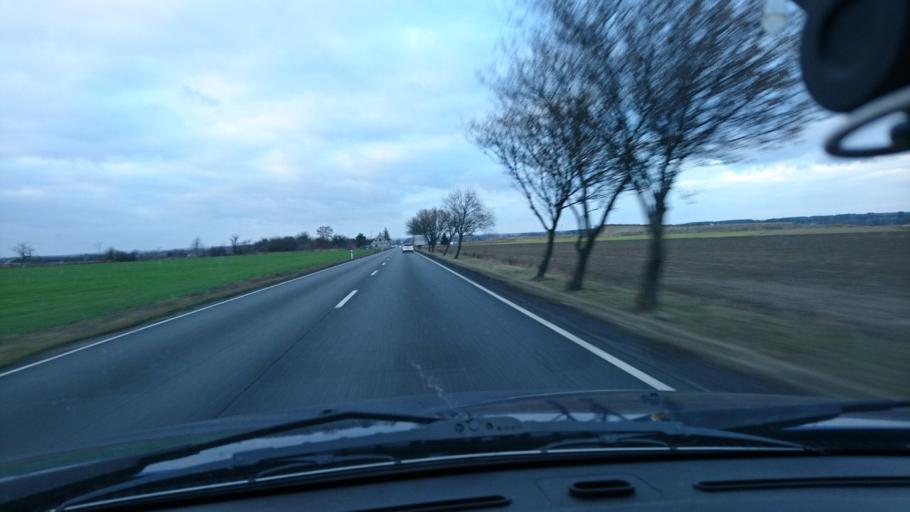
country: PL
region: Greater Poland Voivodeship
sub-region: Powiat kepinski
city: Baranow
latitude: 51.2521
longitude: 18.0138
